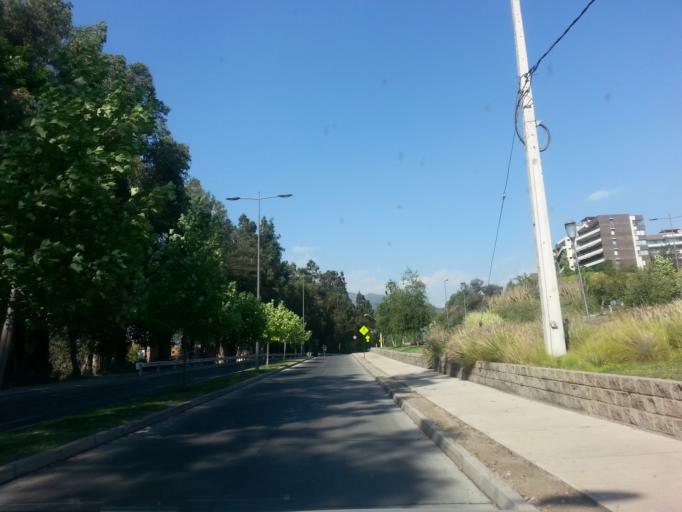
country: CL
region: Santiago Metropolitan
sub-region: Provincia de Santiago
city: Villa Presidente Frei, Nunoa, Santiago, Chile
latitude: -33.3811
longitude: -70.5121
